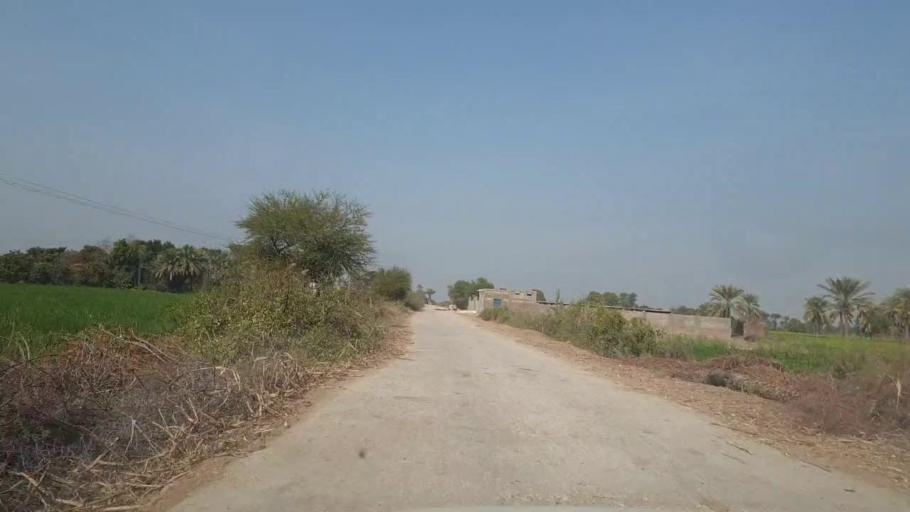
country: PK
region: Sindh
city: Mirpur Khas
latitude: 25.6851
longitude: 69.1552
